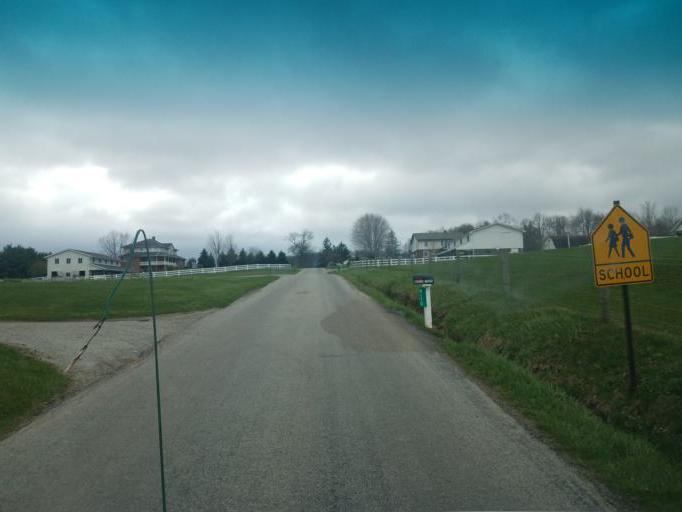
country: US
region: Ohio
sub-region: Stark County
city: Beach City
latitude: 40.6309
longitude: -81.6781
